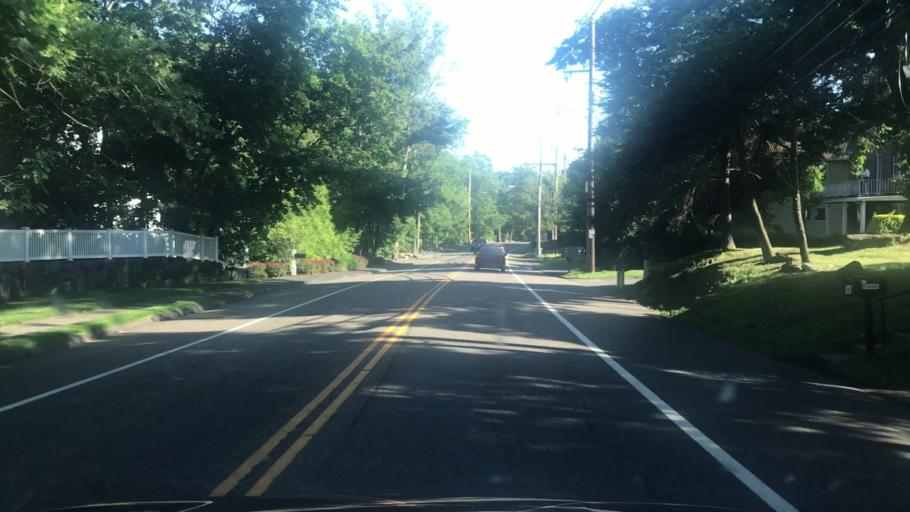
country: US
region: Connecticut
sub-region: Fairfield County
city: Pemberwick
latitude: 41.0205
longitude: -73.6501
